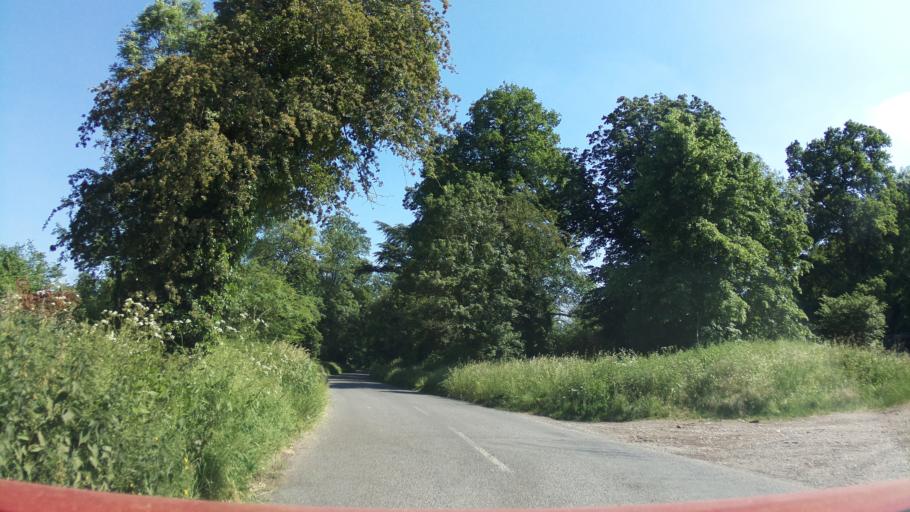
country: GB
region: England
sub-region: Hampshire
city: Abbotts Ann
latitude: 51.2550
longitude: -1.5777
